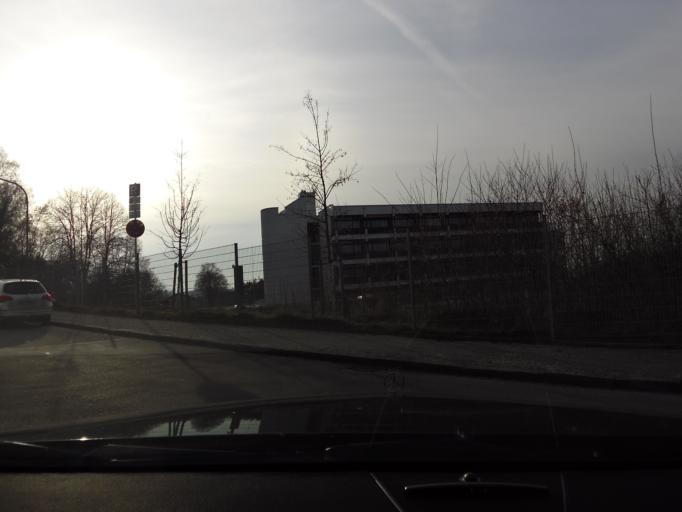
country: DE
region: Bavaria
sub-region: Lower Bavaria
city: Landshut
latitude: 48.5231
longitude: 12.1512
